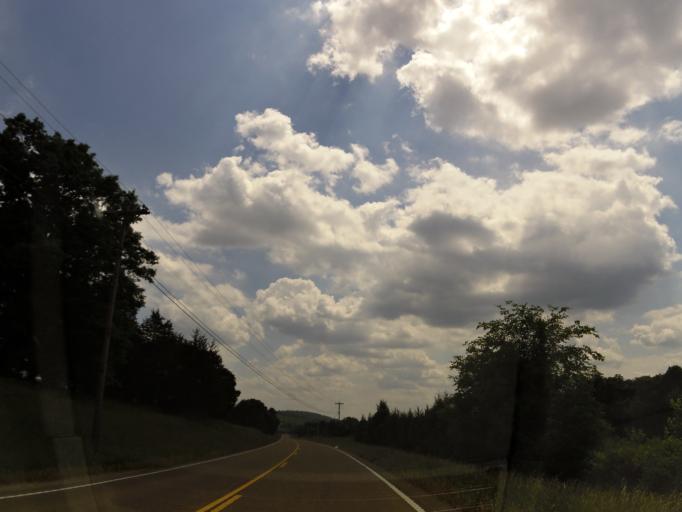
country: US
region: Tennessee
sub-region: Bledsoe County
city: Pikeville
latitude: 35.5532
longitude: -85.2528
